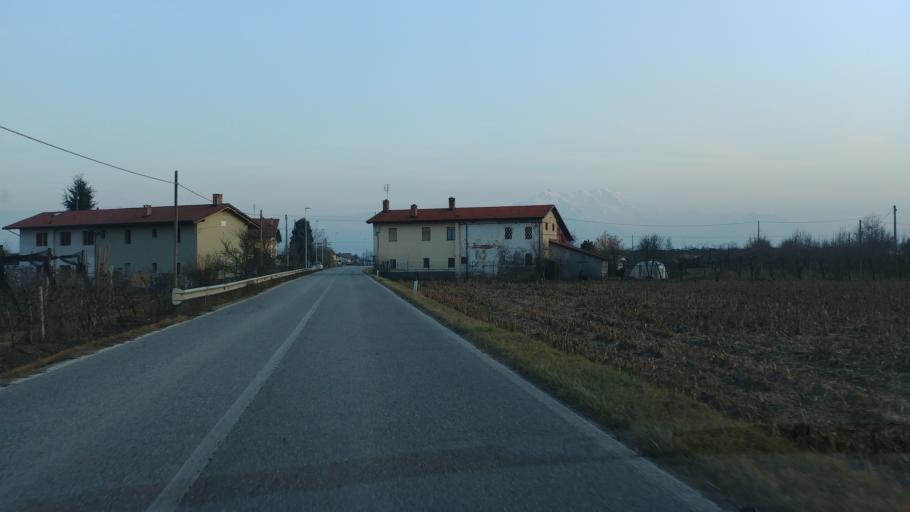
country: IT
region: Piedmont
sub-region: Provincia di Cuneo
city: San Defendente
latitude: 44.4134
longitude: 7.5136
